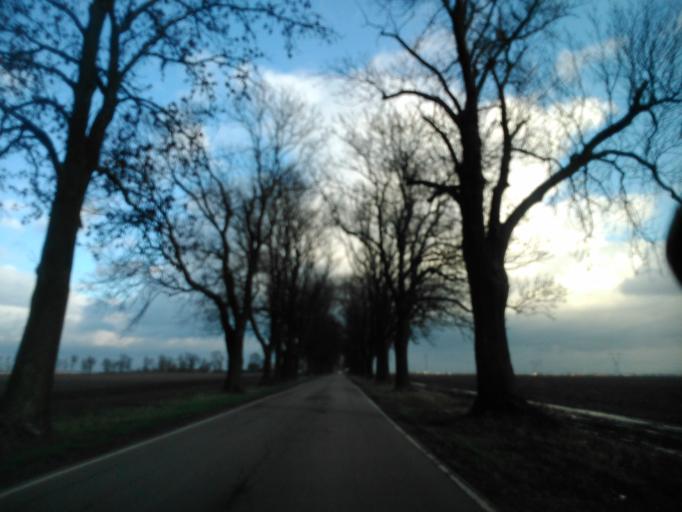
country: PL
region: Masovian Voivodeship
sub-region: Powiat warszawski zachodni
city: Leszno
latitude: 52.2430
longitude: 20.5961
